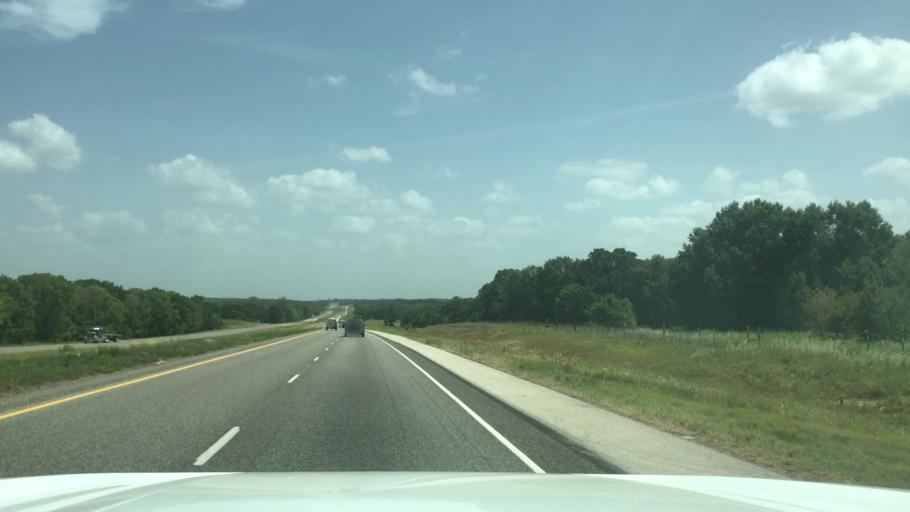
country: US
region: Texas
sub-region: Robertson County
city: Calvert
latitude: 30.9544
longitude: -96.6542
